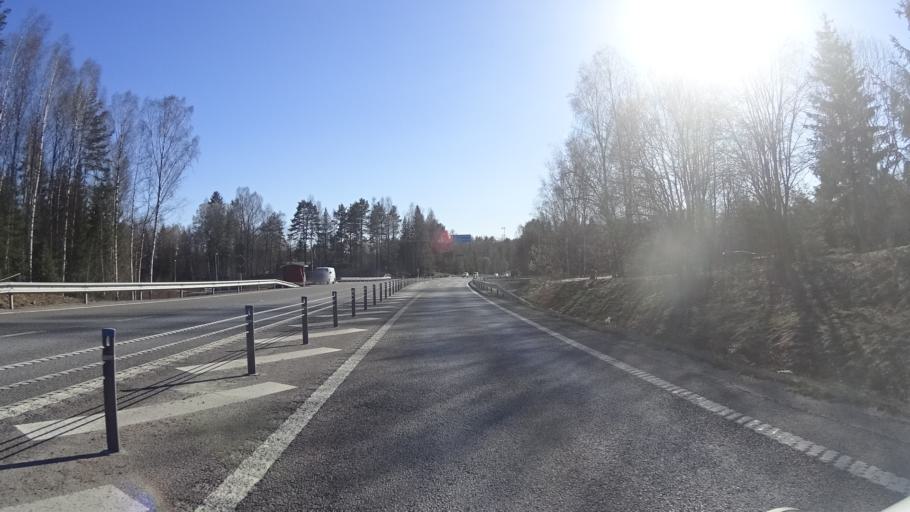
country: SE
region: Vaermland
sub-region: Arvika Kommun
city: Arvika
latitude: 59.6489
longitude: 12.7501
